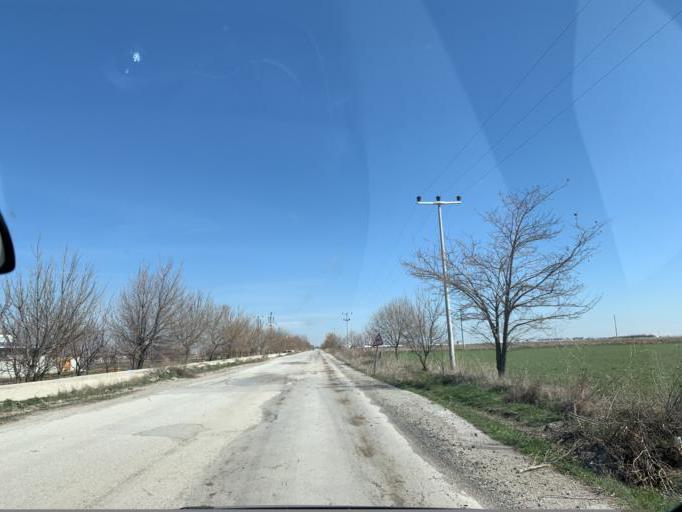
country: TR
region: Konya
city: Catalhoeyuek
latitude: 37.7463
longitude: 32.8257
